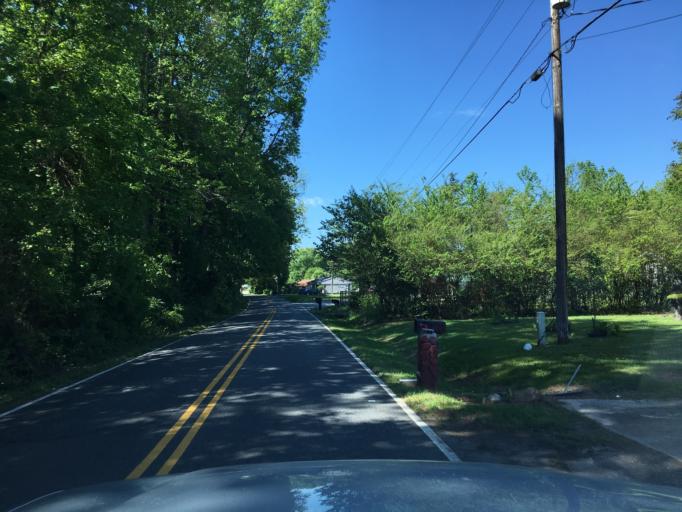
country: US
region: South Carolina
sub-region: Spartanburg County
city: Southern Shops
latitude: 34.9959
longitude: -82.0184
